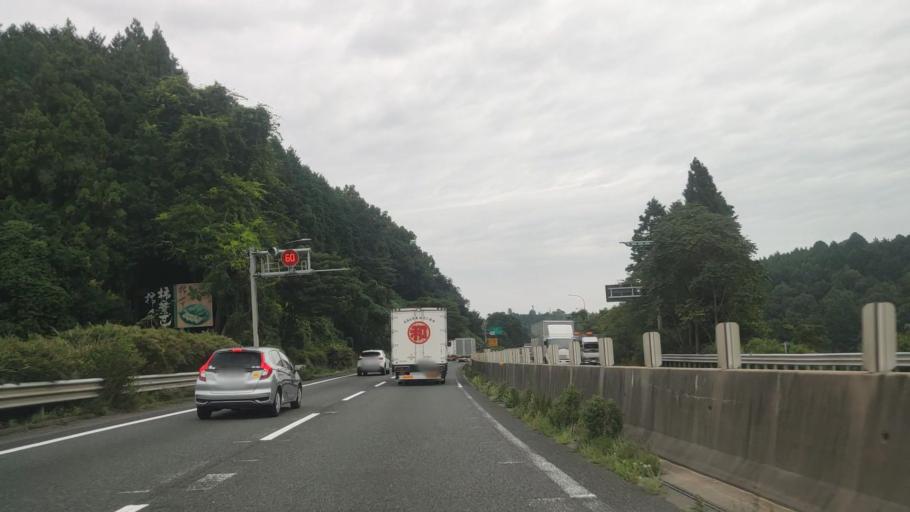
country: JP
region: Mie
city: Nabari
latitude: 34.6779
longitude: 136.0348
